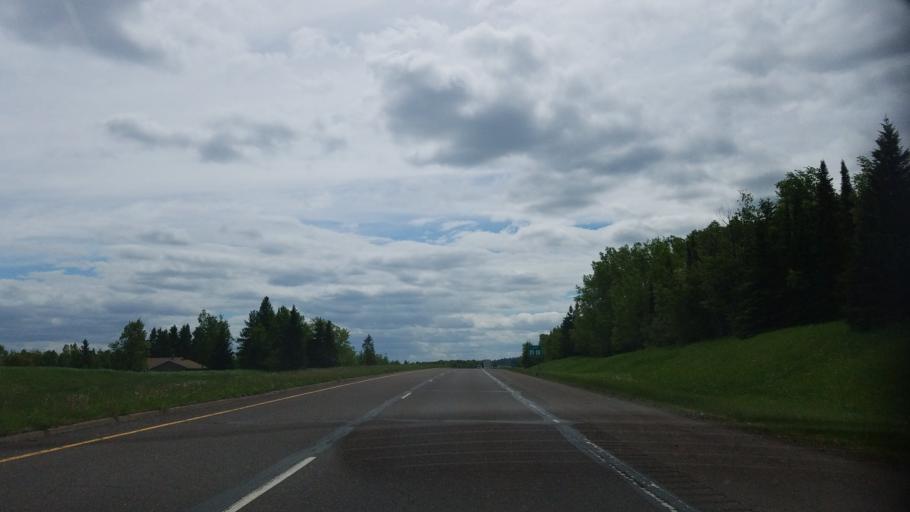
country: US
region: Minnesota
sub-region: Lake County
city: Two Harbors
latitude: 47.0152
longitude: -91.7051
